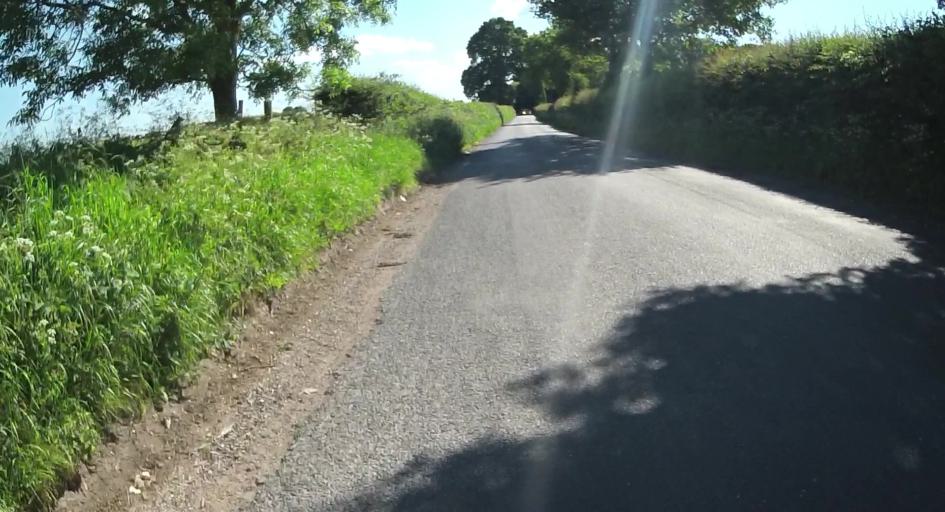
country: GB
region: England
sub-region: Hampshire
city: Old Basing
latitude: 51.2114
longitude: -1.0219
